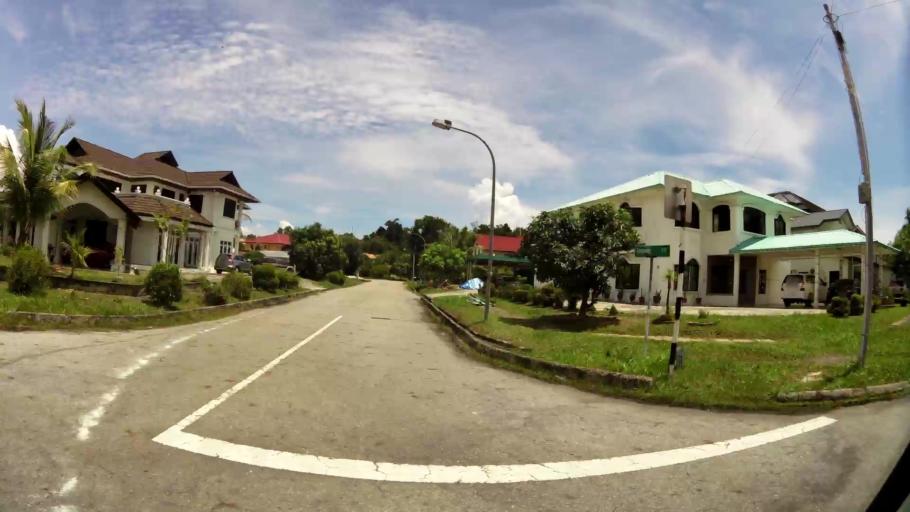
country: BN
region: Brunei and Muara
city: Bandar Seri Begawan
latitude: 4.9625
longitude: 114.9105
